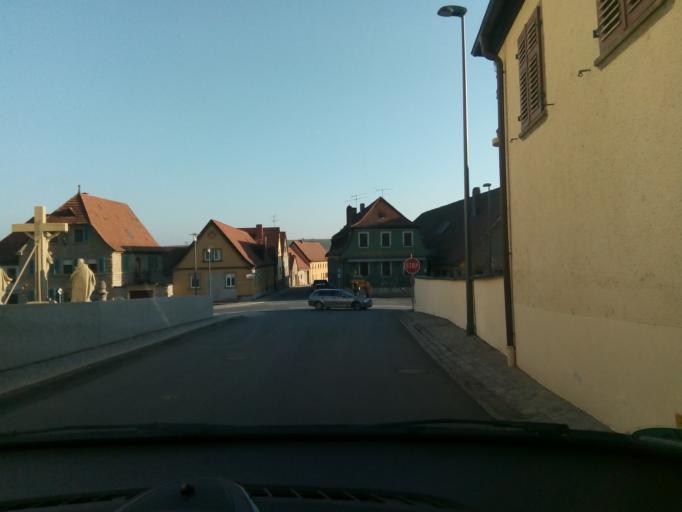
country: DE
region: Bavaria
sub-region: Regierungsbezirk Unterfranken
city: Nordheim
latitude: 49.8626
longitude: 10.1744
